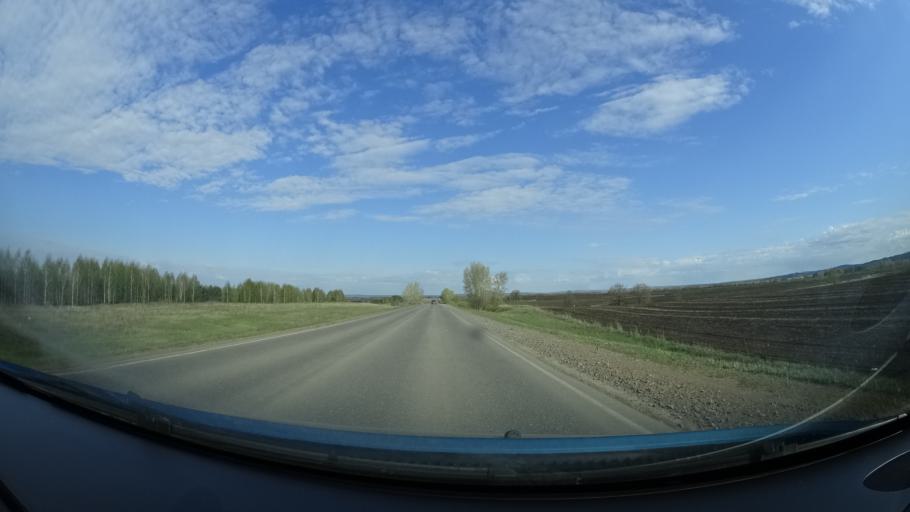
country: RU
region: Bashkortostan
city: Blagoveshchensk
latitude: 55.1905
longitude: 55.8409
